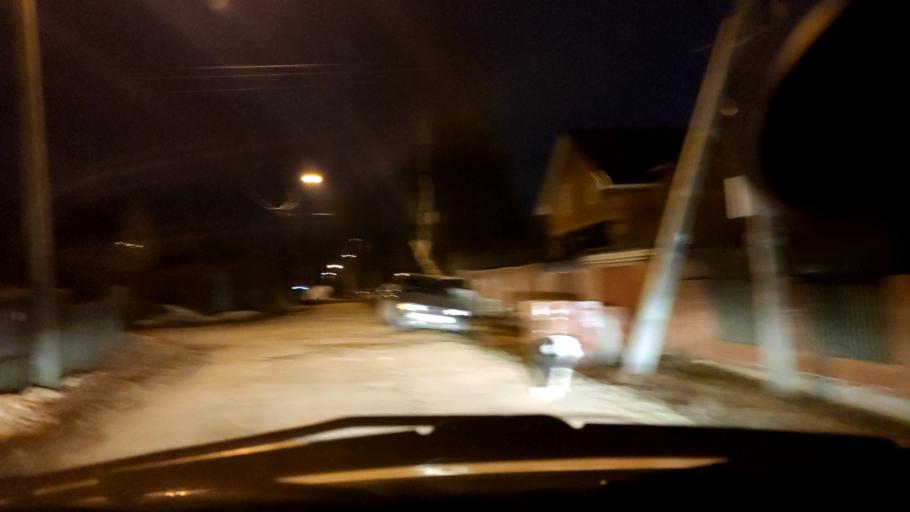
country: RU
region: Bashkortostan
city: Iglino
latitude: 54.7884
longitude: 56.2299
